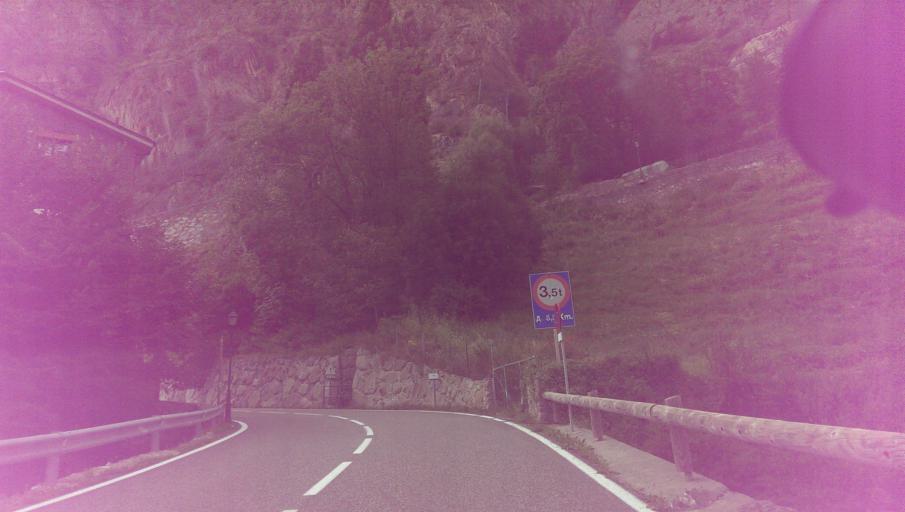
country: AD
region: Canillo
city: Canillo
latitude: 42.5667
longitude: 1.5957
